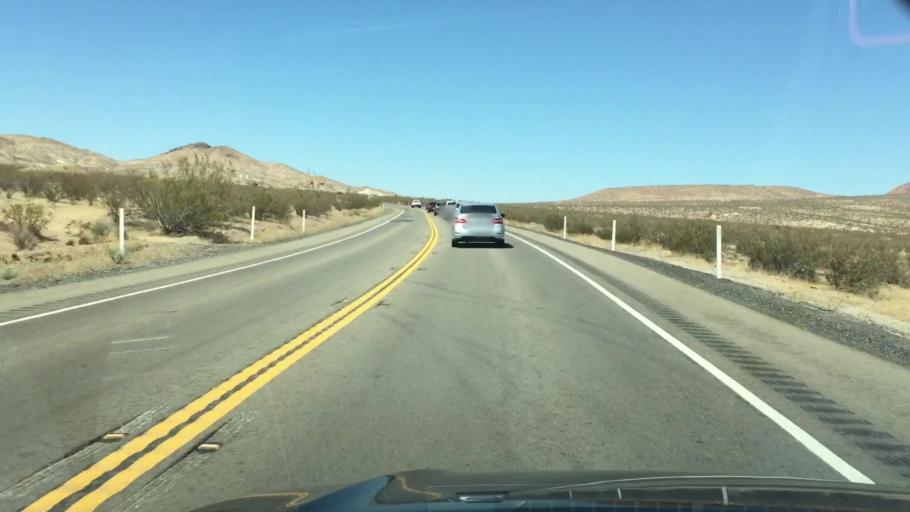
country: US
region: California
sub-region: Kern County
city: Ridgecrest
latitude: 35.3339
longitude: -117.6187
